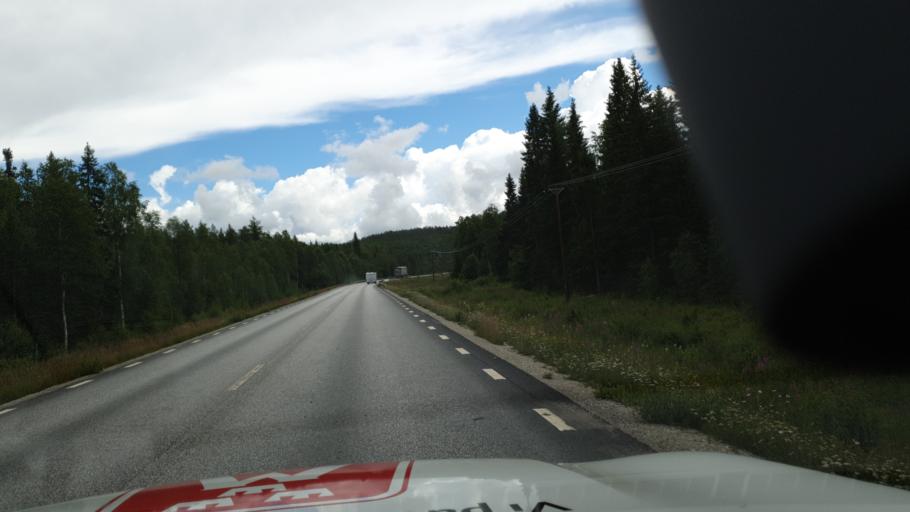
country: SE
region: Vaesterbotten
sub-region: Vannas Kommun
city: Vaennaes
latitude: 64.0466
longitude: 19.6823
